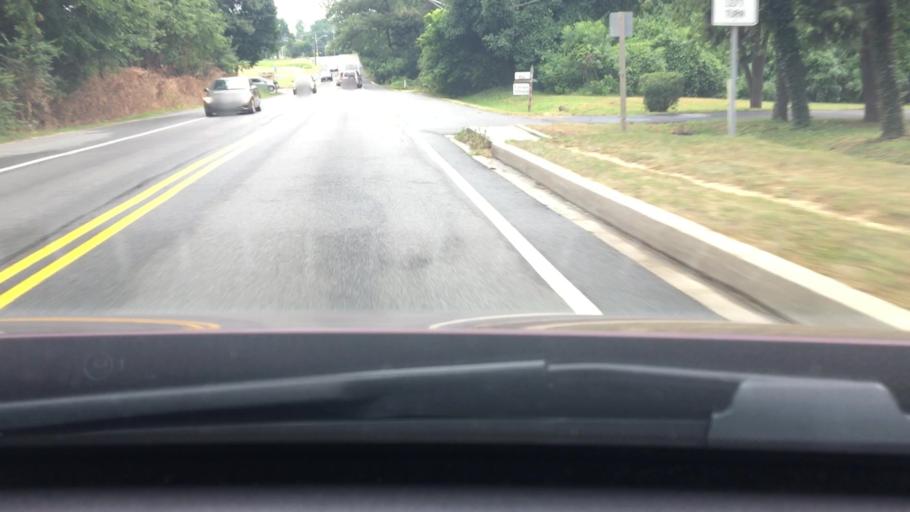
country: US
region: Maryland
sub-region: Prince George's County
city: Calverton
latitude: 39.0593
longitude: -76.9215
